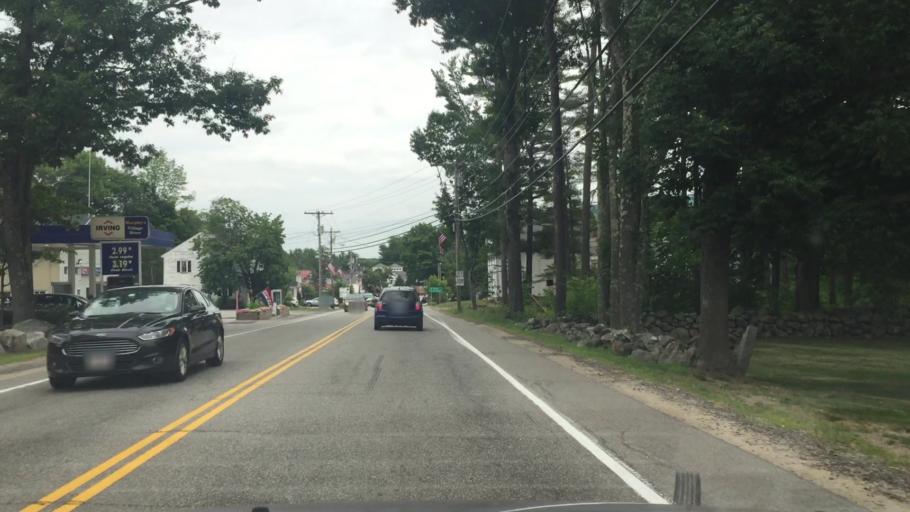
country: US
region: New Hampshire
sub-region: Carroll County
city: Moultonborough
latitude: 43.7529
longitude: -71.3986
